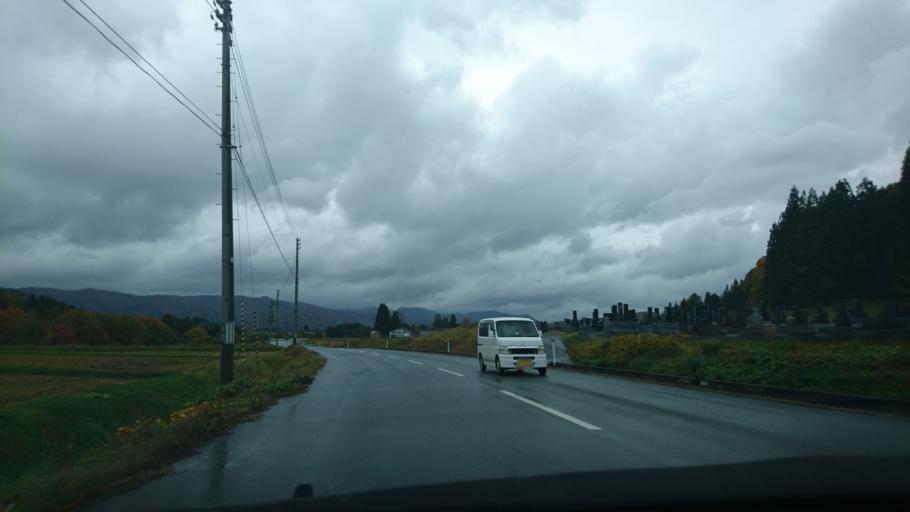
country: JP
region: Akita
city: Yokotemachi
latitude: 39.3829
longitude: 140.7663
